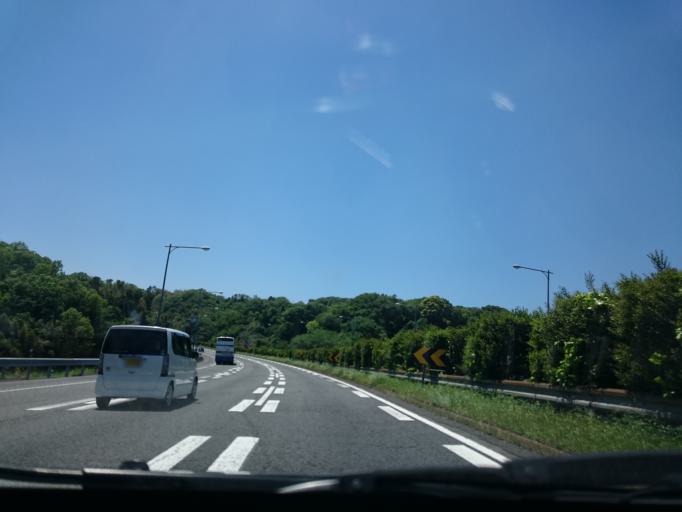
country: JP
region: Kanagawa
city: Hadano
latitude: 35.3497
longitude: 139.2063
